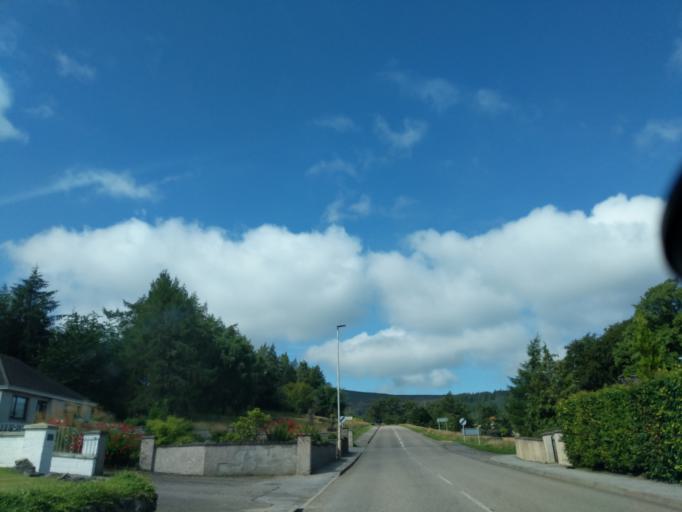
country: GB
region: Scotland
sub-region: Moray
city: Dufftown
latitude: 57.4443
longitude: -3.1347
